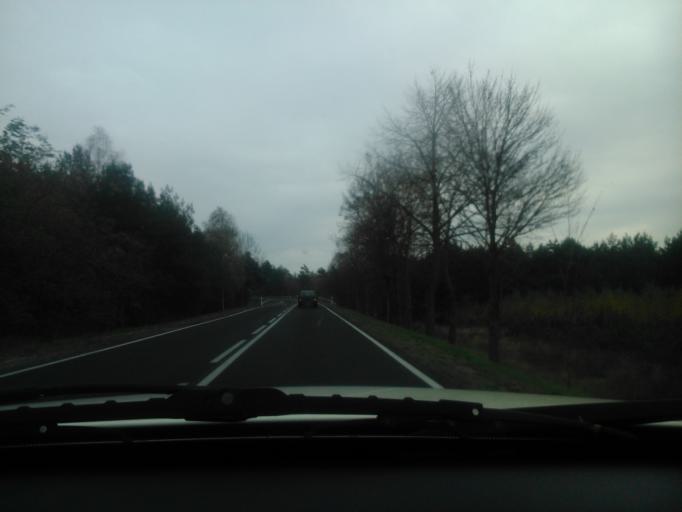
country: PL
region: Warmian-Masurian Voivodeship
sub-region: Powiat dzialdowski
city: Ilowo -Osada
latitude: 53.1149
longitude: 20.2650
